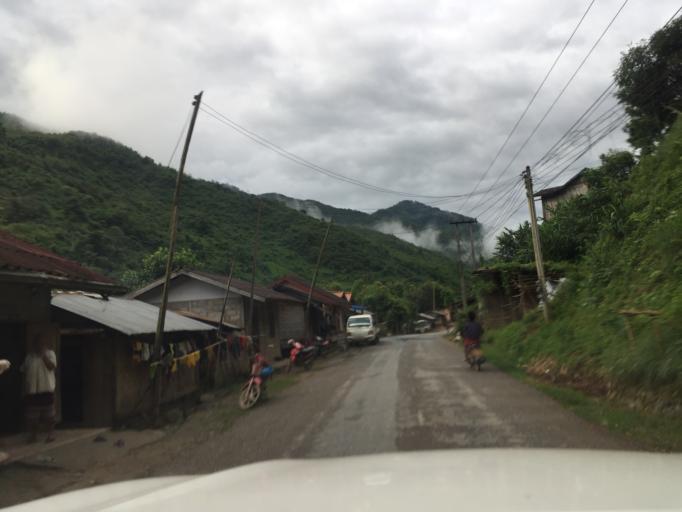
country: LA
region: Oudomxai
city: Muang La
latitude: 21.0535
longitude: 102.2408
